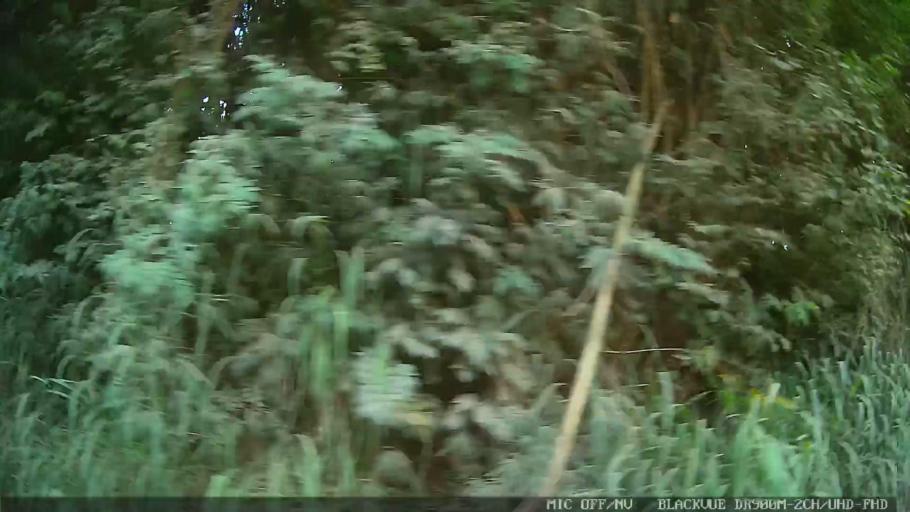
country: BR
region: Sao Paulo
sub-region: Atibaia
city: Atibaia
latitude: -23.1194
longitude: -46.6211
